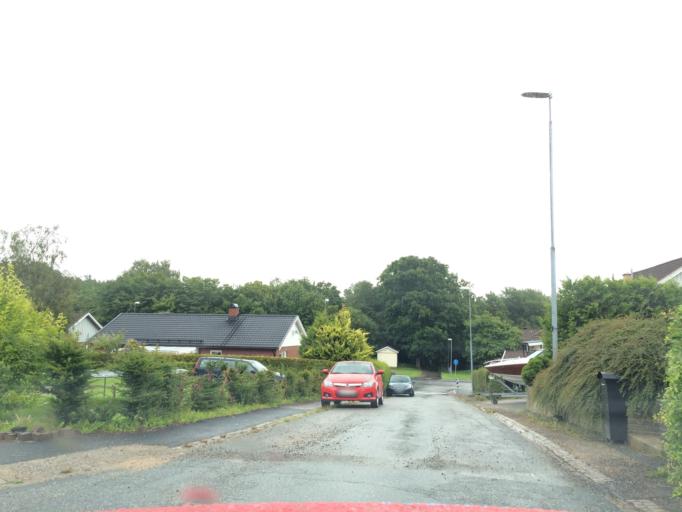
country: SE
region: Vaestra Goetaland
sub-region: Trollhattan
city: Trollhattan
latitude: 58.2848
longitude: 12.2597
